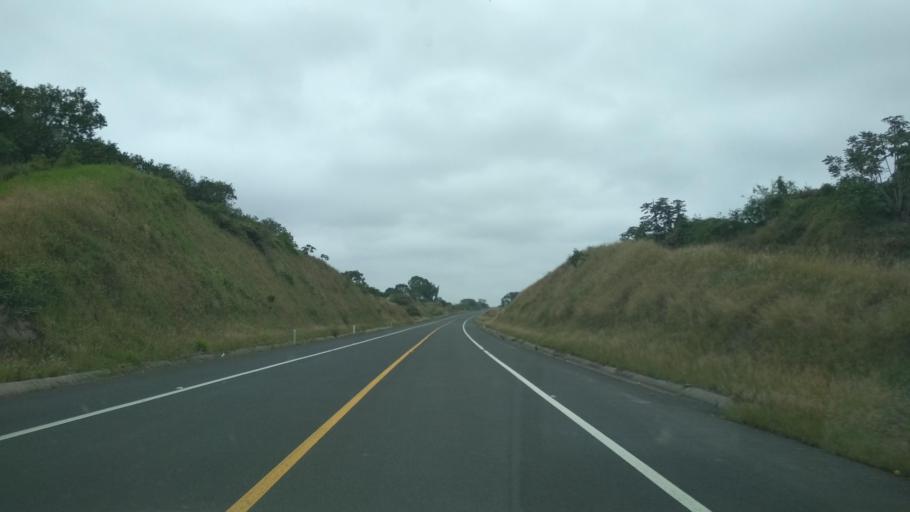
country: MX
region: Veracruz
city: Vega de San Marcos
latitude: 20.1776
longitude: -96.9636
